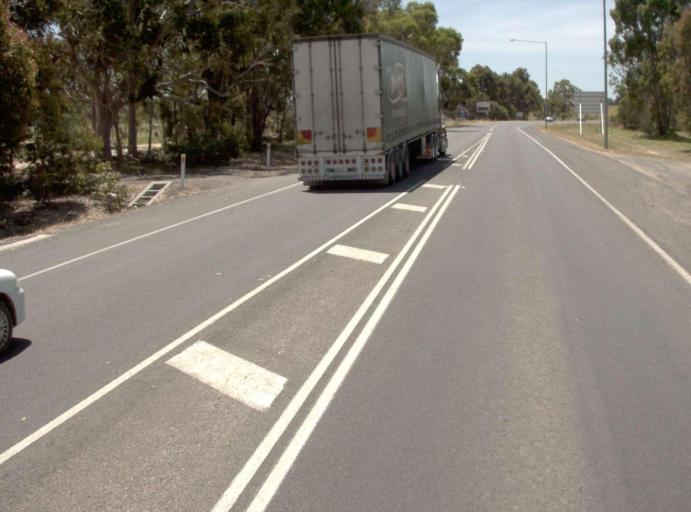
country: AU
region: Victoria
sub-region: East Gippsland
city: Bairnsdale
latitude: -37.8083
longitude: 147.6487
